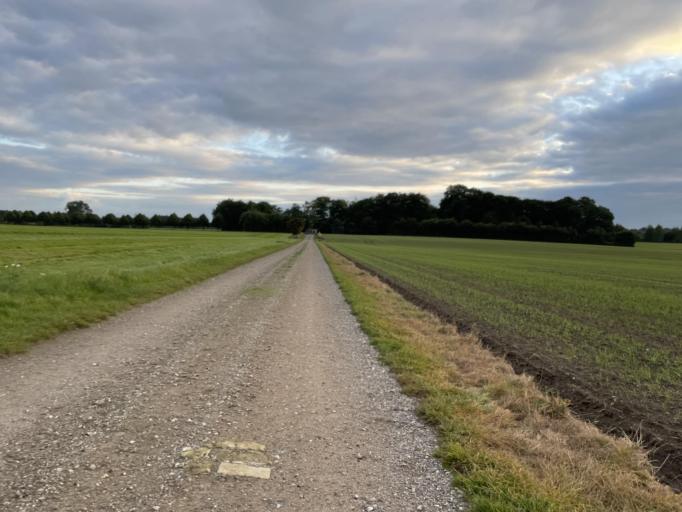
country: DK
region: South Denmark
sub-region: Kerteminde Kommune
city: Langeskov
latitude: 55.3977
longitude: 10.5885
